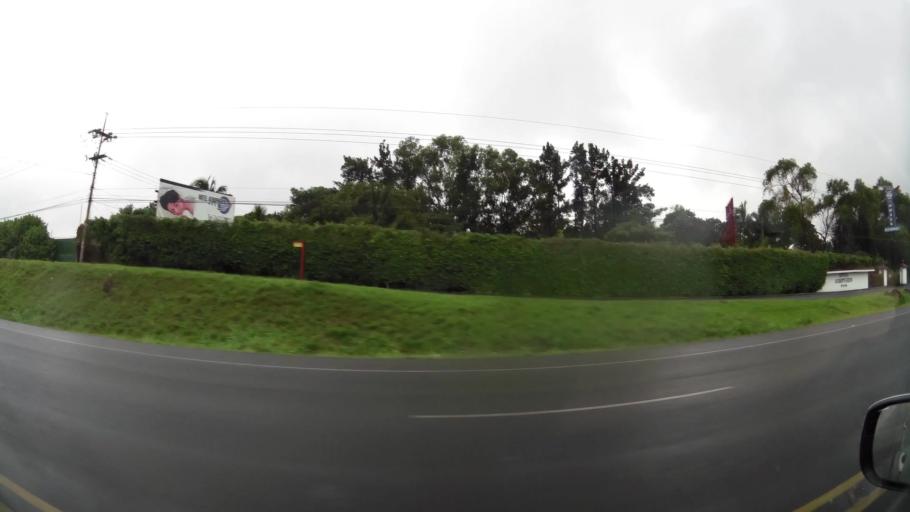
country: CR
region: Alajuela
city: Alajuela
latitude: 9.9938
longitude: -84.2414
